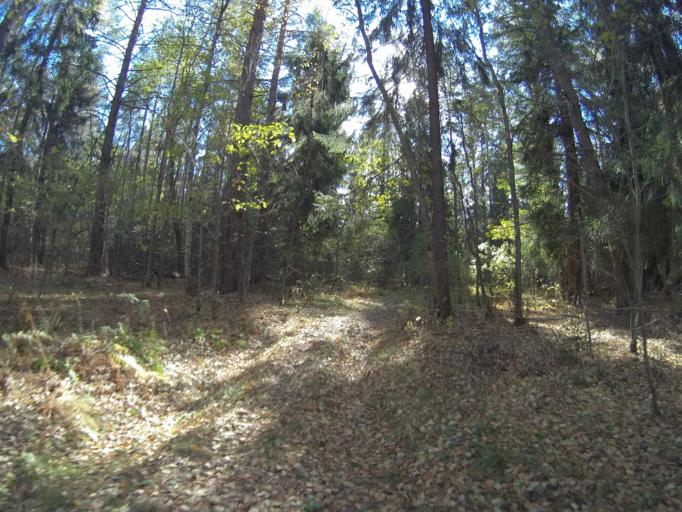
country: RU
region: Vladimir
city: Kommunar
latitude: 56.0326
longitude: 40.4937
